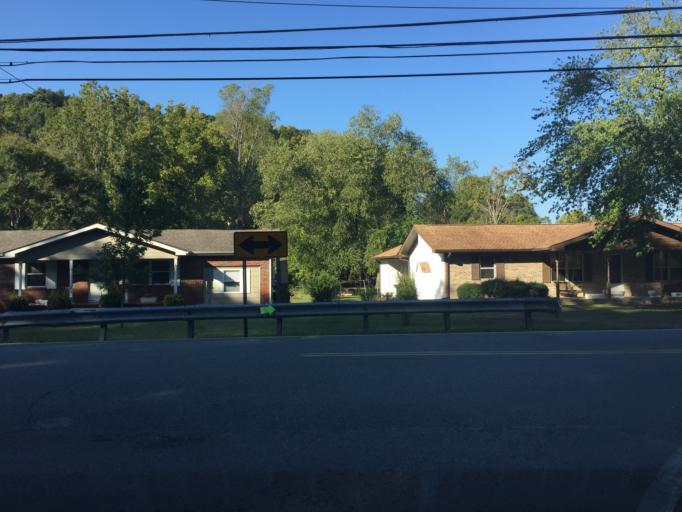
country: US
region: Tennessee
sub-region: Hamilton County
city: Harrison
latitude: 35.1181
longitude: -85.1184
